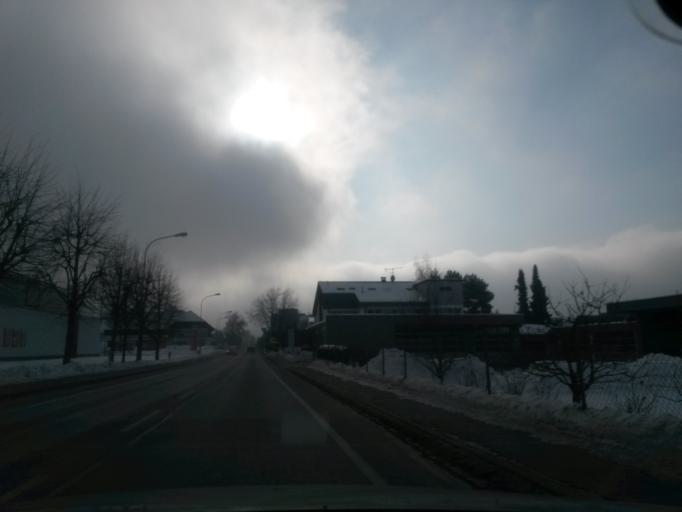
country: AT
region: Vorarlberg
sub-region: Politischer Bezirk Bregenz
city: Lochau
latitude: 47.5364
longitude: 9.7522
